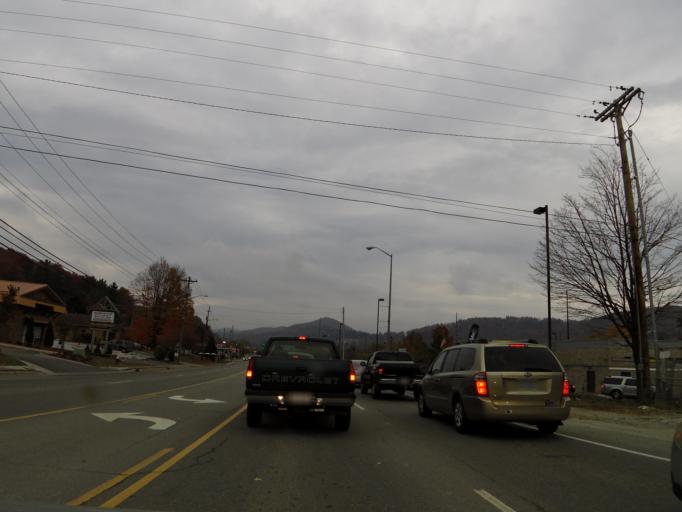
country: US
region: North Carolina
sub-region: Watauga County
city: Boone
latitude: 36.2068
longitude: -81.6714
